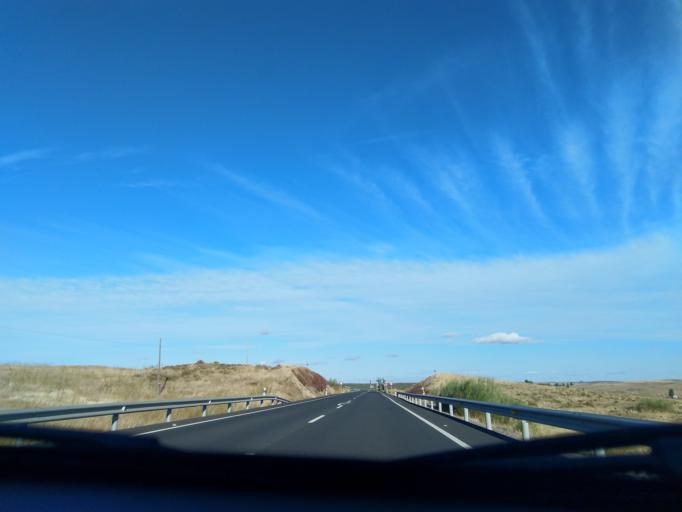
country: ES
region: Extremadura
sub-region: Provincia de Badajoz
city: Ahillones
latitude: 38.2684
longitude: -5.8427
